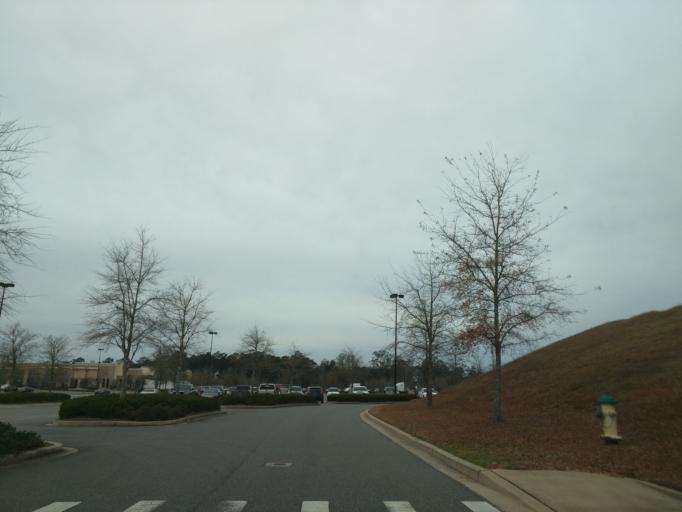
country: US
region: Florida
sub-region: Leon County
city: Tallahassee
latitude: 30.4620
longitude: -84.2138
